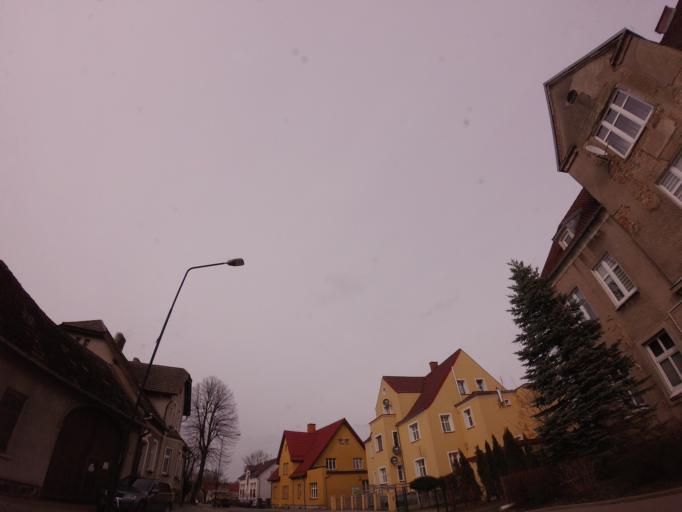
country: PL
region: West Pomeranian Voivodeship
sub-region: Powiat drawski
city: Drawsko Pomorskie
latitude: 53.5248
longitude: 15.8158
